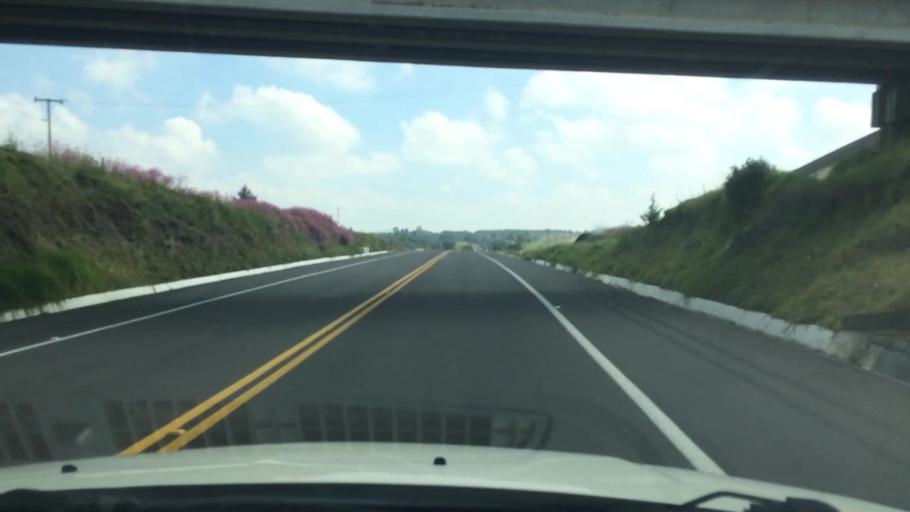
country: MX
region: Mexico
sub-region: Villa Victoria
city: Colonia Doctor Gustavo Baz
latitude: 19.3734
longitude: -99.9138
